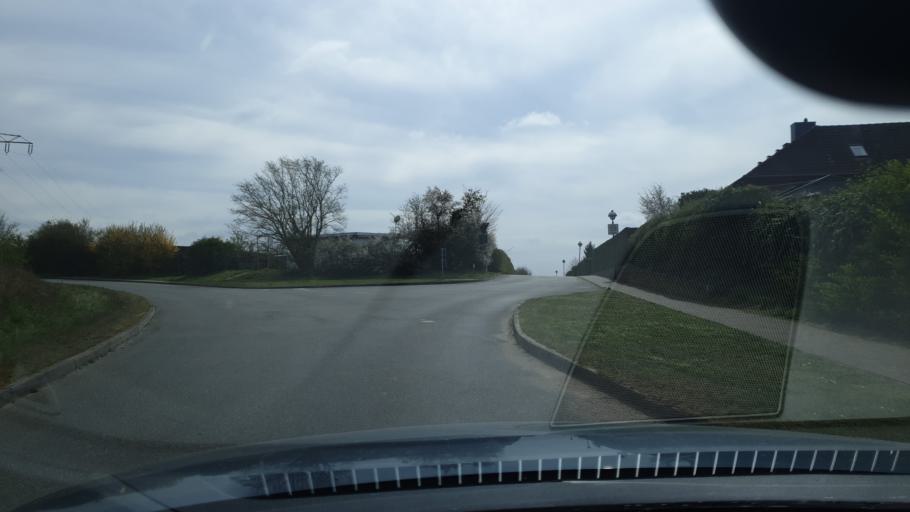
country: DE
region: Mecklenburg-Vorpommern
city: Wittenforden
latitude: 53.6332
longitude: 11.3175
